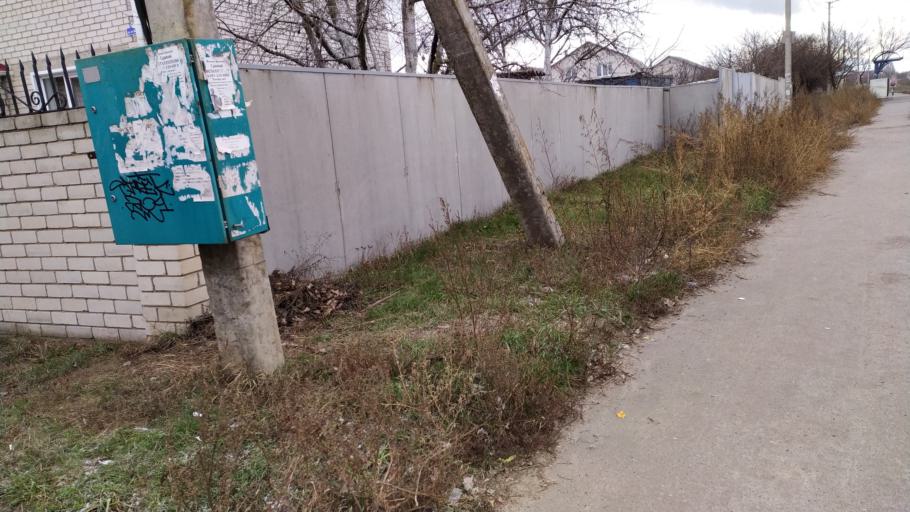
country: RU
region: Kursk
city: Kursk
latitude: 51.6373
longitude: 36.1387
